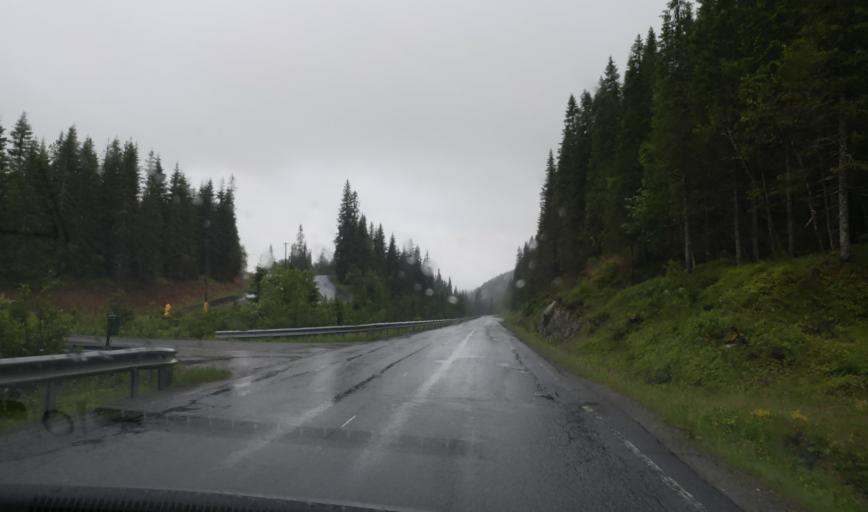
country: NO
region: Sor-Trondelag
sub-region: Selbu
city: Mebonden
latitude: 63.3346
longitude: 11.0931
